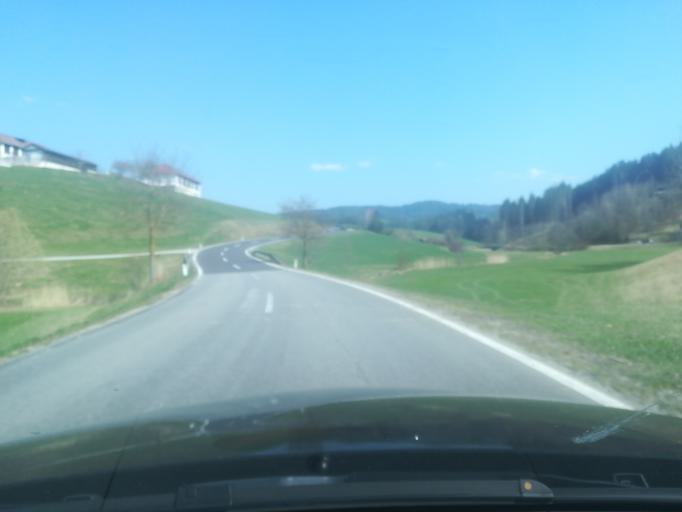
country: AT
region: Upper Austria
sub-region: Politischer Bezirk Perg
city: Perg
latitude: 48.3543
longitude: 14.6754
